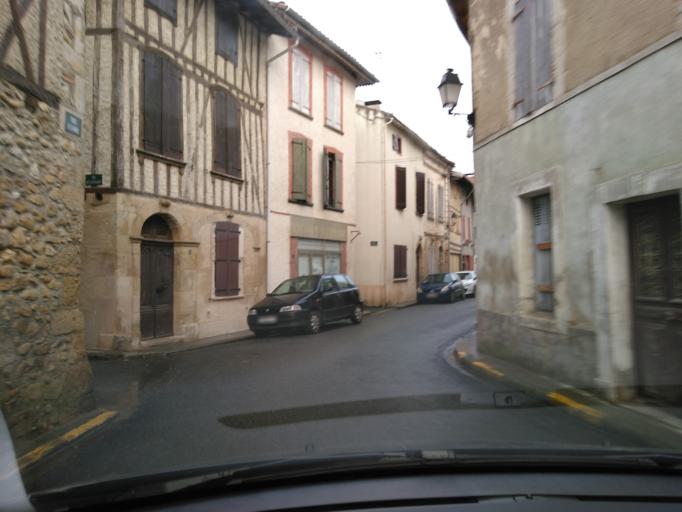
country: FR
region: Midi-Pyrenees
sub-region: Departement de la Haute-Garonne
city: Montesquieu-Volvestre
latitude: 43.1430
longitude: 1.3077
